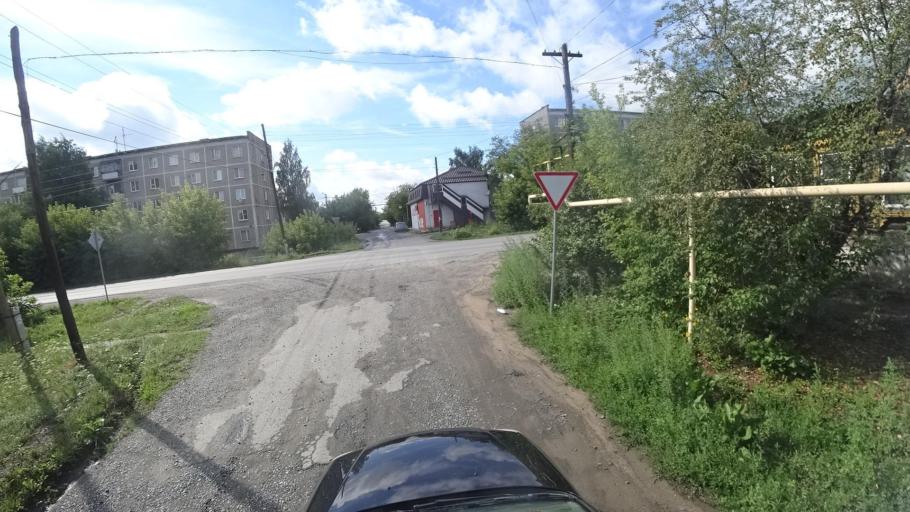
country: RU
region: Sverdlovsk
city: Kamyshlov
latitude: 56.8419
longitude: 62.7203
